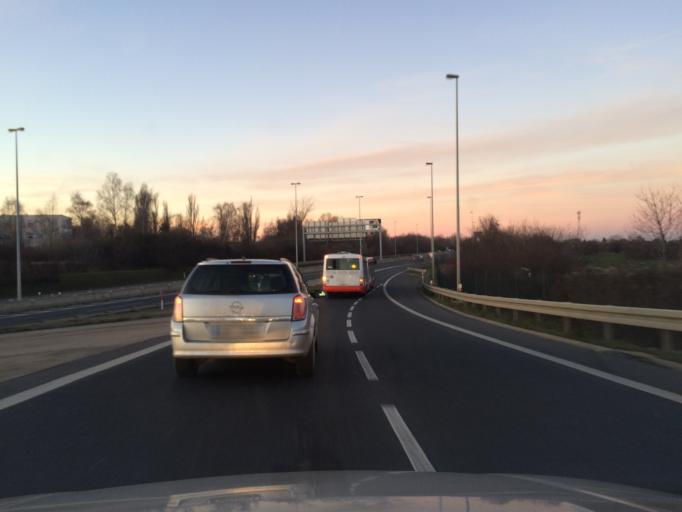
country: CZ
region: Central Bohemia
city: Hostivice
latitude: 50.0951
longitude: 14.2968
